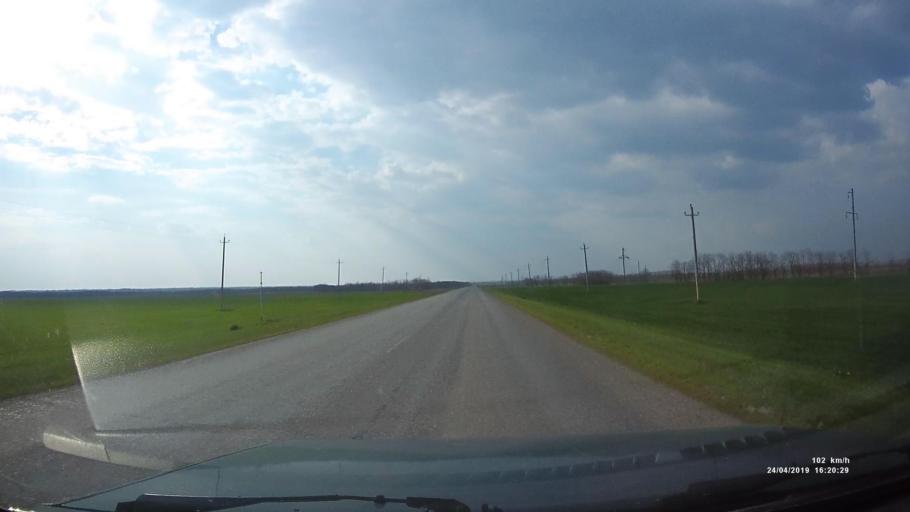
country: RU
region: Rostov
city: Orlovskiy
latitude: 46.7935
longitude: 42.0787
